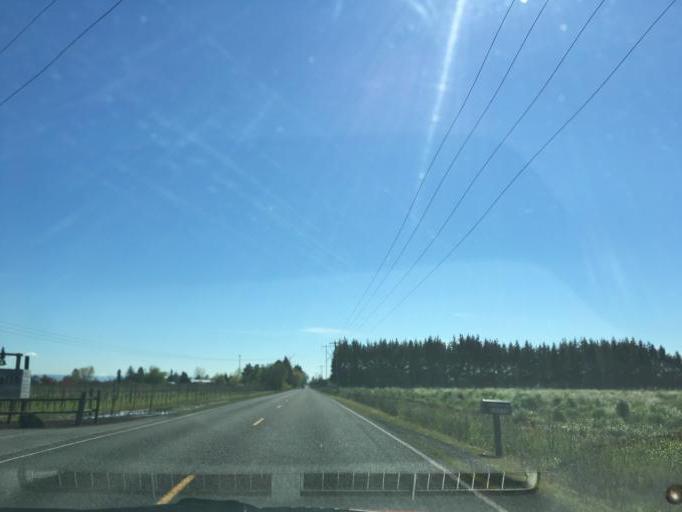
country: US
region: Oregon
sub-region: Marion County
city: Hubbard
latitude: 45.1804
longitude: -122.7226
